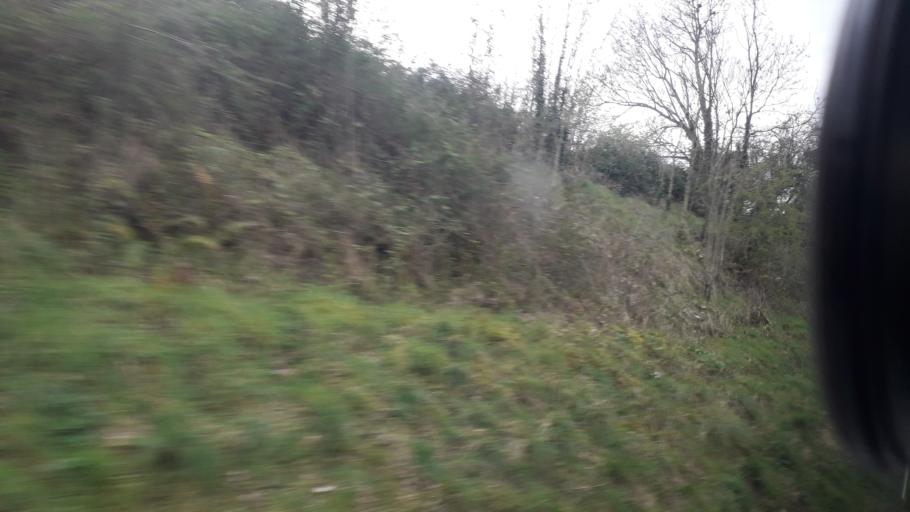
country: IE
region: Leinster
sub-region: An Longfort
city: Longford
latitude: 53.7255
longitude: -7.7736
